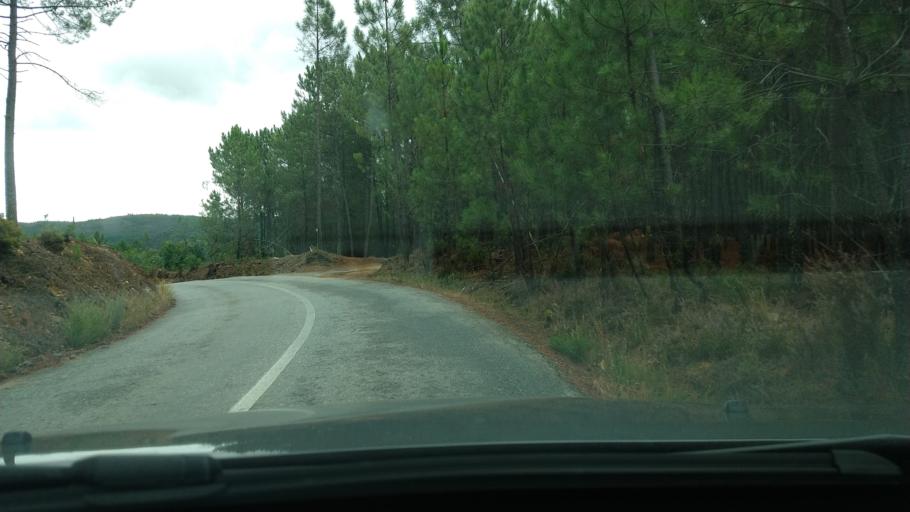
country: PT
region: Castelo Branco
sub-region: Concelho do Fundao
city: Aldeia de Joanes
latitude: 40.2206
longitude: -7.6327
